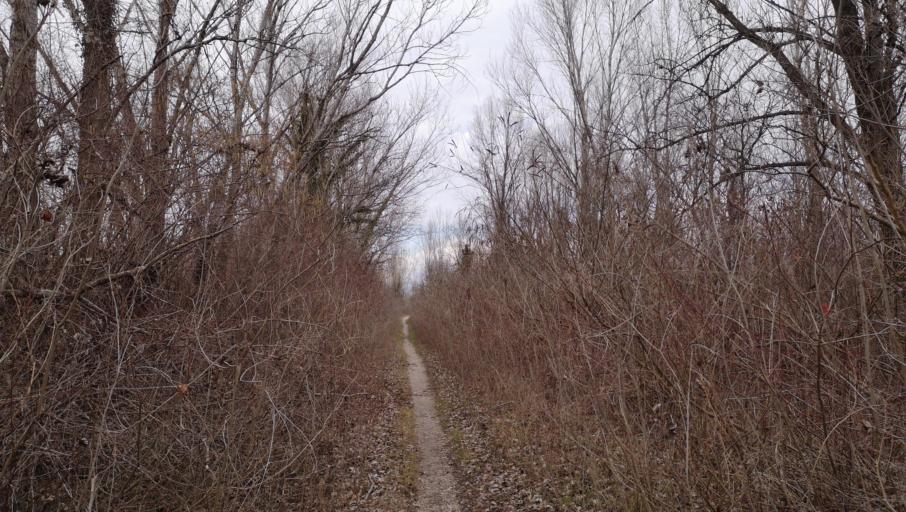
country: IT
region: Friuli Venezia Giulia
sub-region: Provincia di Udine
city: Povoletto
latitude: 46.1059
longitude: 13.2776
